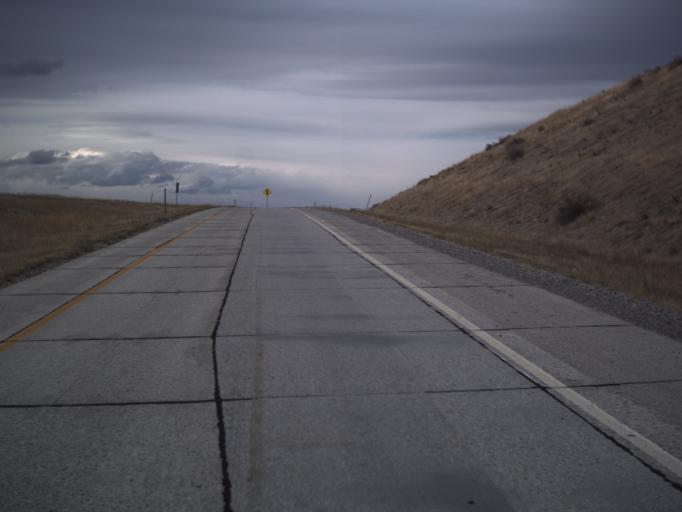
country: US
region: Idaho
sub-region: Oneida County
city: Malad City
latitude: 41.9779
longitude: -112.1898
